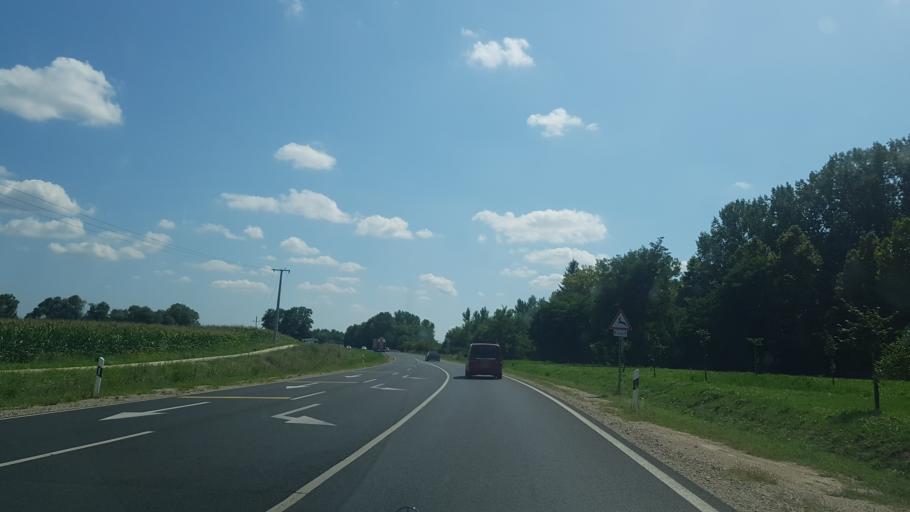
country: HU
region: Somogy
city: Marcali
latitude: 46.5600
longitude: 17.4118
